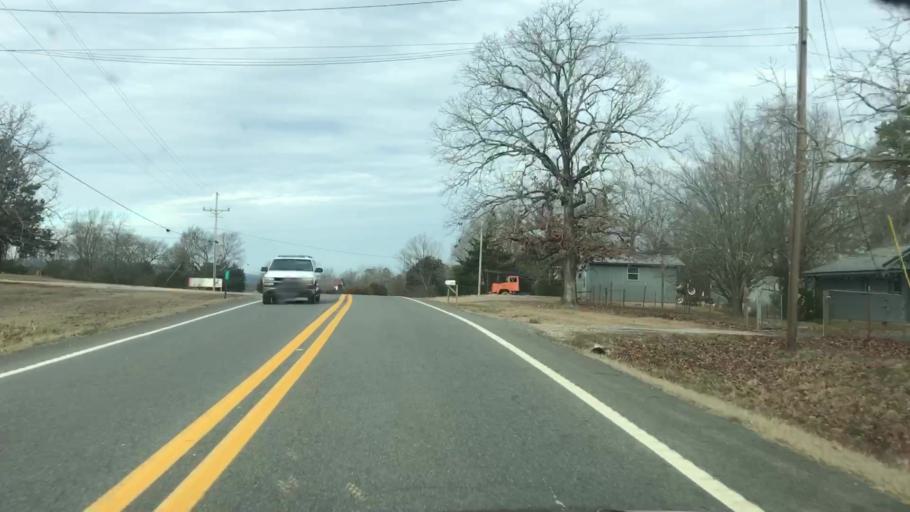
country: US
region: Arkansas
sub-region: Montgomery County
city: Mount Ida
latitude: 34.6242
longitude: -93.7277
